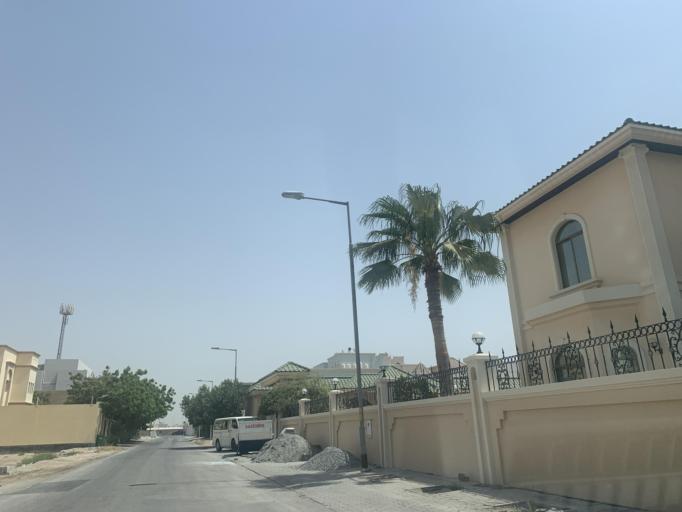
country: BH
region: Manama
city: Jidd Hafs
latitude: 26.1998
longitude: 50.5051
